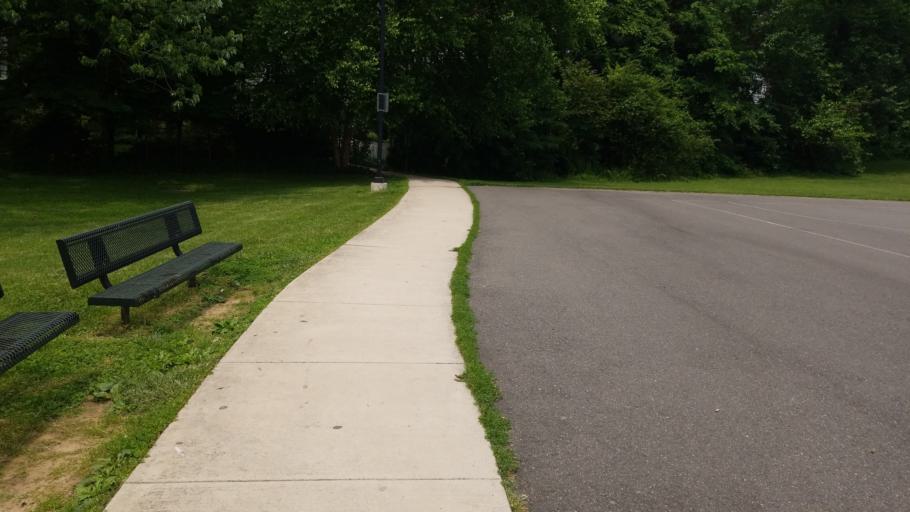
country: US
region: Virginia
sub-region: Fairfax County
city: Seven Corners
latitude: 38.8877
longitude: -77.1415
